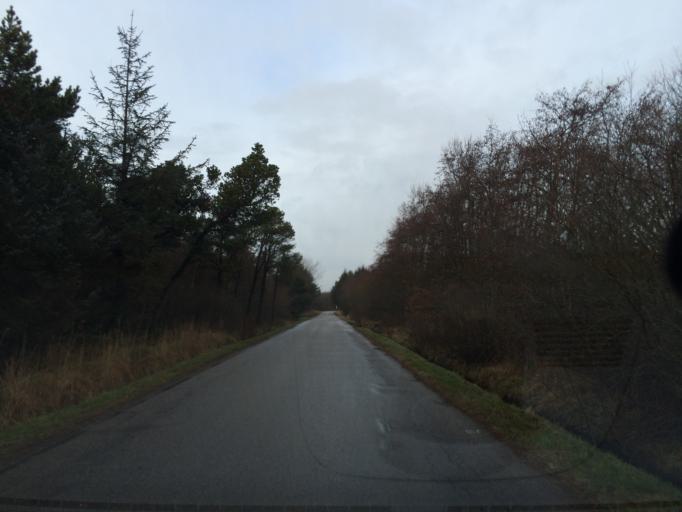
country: DK
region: Central Jutland
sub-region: Holstebro Kommune
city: Ulfborg
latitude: 56.2679
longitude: 8.1517
